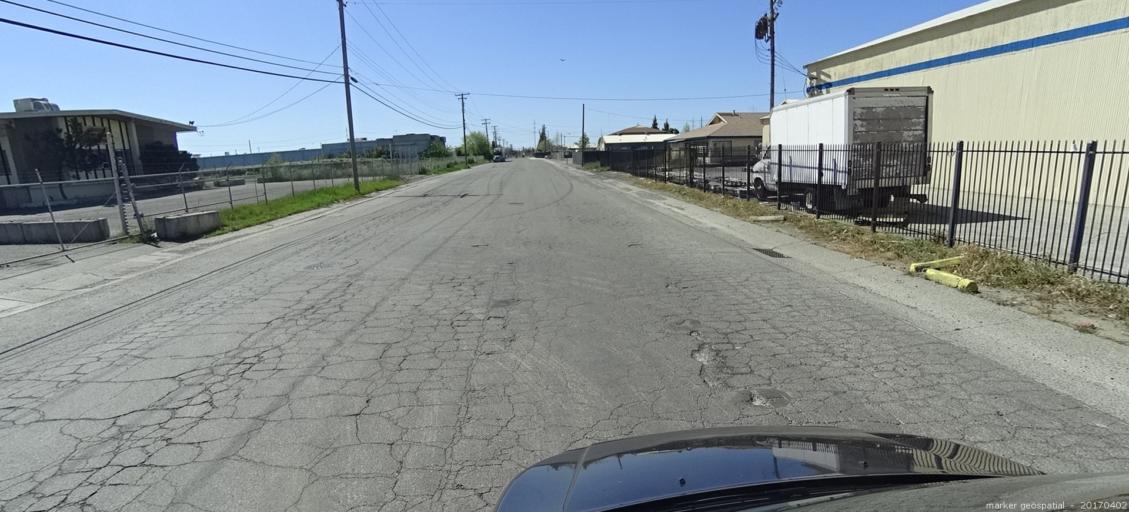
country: US
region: California
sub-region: Sacramento County
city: Parkway
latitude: 38.5032
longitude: -121.4659
